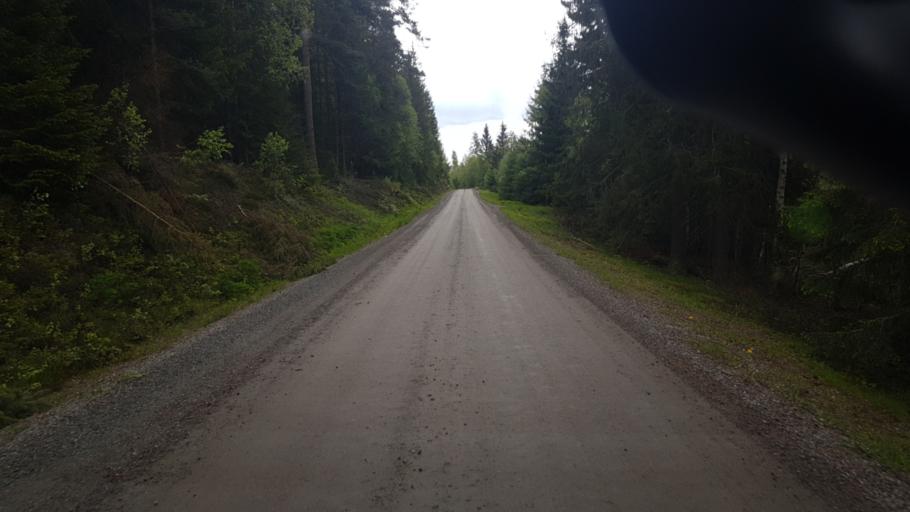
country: NO
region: Ostfold
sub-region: Romskog
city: Romskog
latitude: 59.7090
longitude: 12.0392
